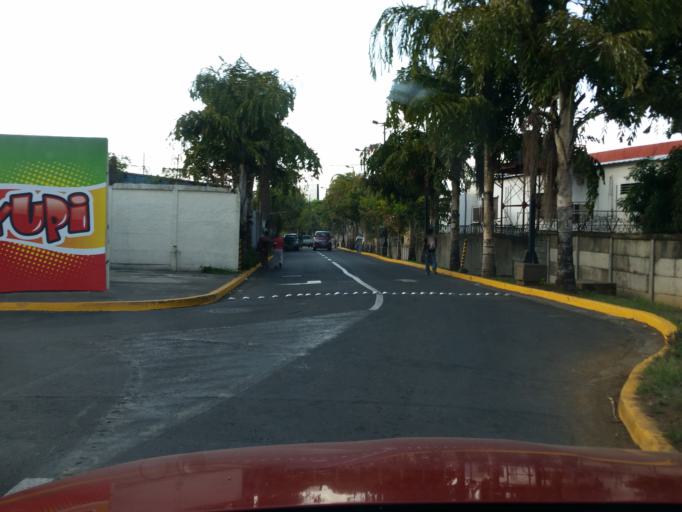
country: NI
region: Managua
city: Managua
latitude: 12.1283
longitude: -86.2639
